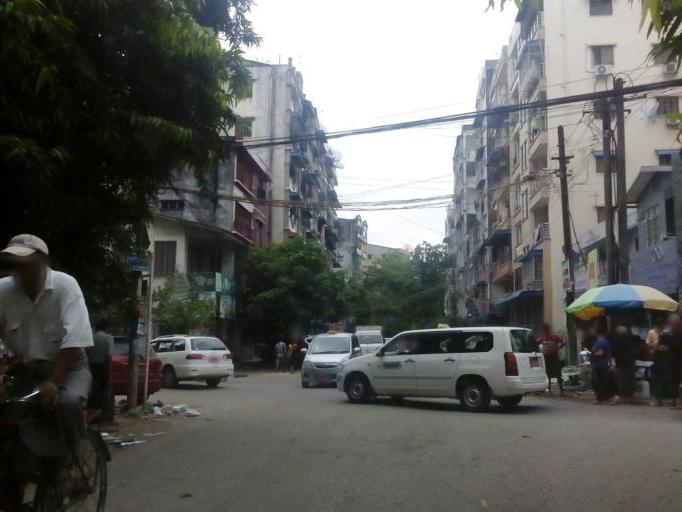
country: MM
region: Yangon
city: Yangon
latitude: 16.8032
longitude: 96.1767
